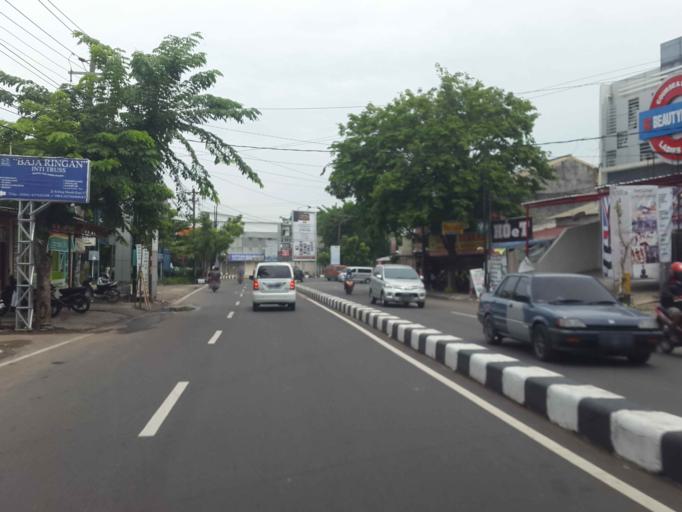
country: ID
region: Central Java
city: Semarang
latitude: -7.0234
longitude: 110.4622
